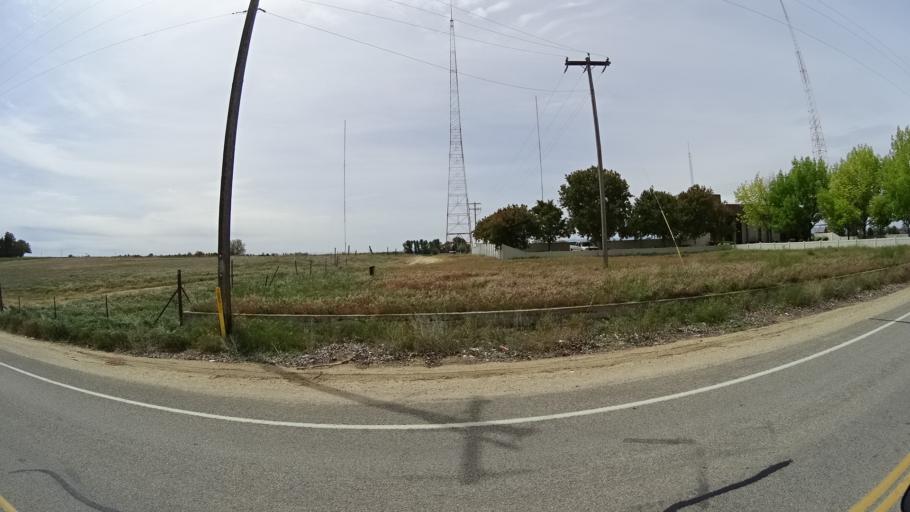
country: US
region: Idaho
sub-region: Ada County
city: Meridian
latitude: 43.5611
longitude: -116.3988
